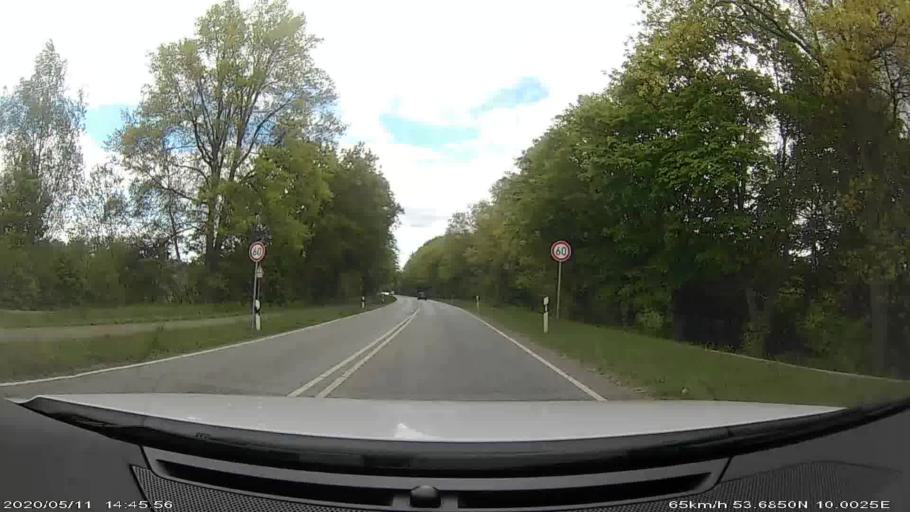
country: DE
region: Schleswig-Holstein
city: Norderstedt
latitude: 53.6994
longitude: 10.0118
